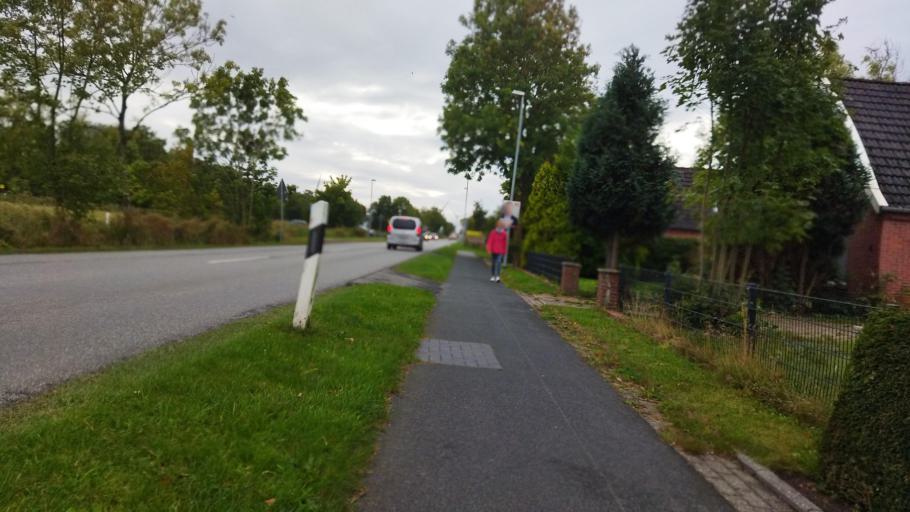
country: DE
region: Lower Saxony
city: Wirdum
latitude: 53.4654
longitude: 7.1328
